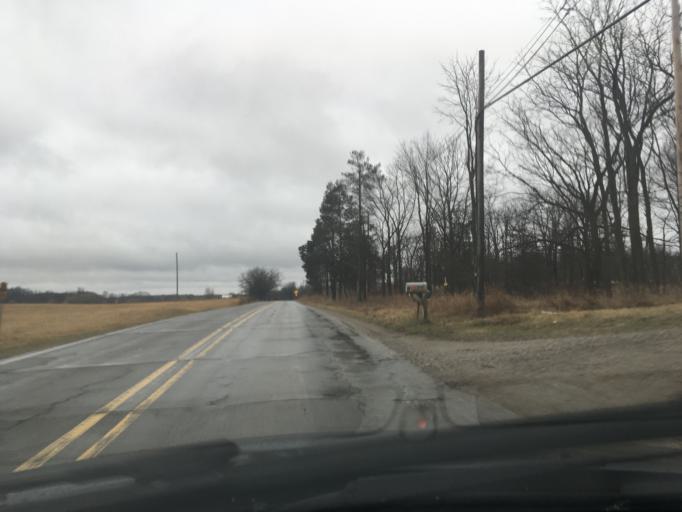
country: US
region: Michigan
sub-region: Jackson County
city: Grass Lake
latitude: 42.3101
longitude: -84.1347
